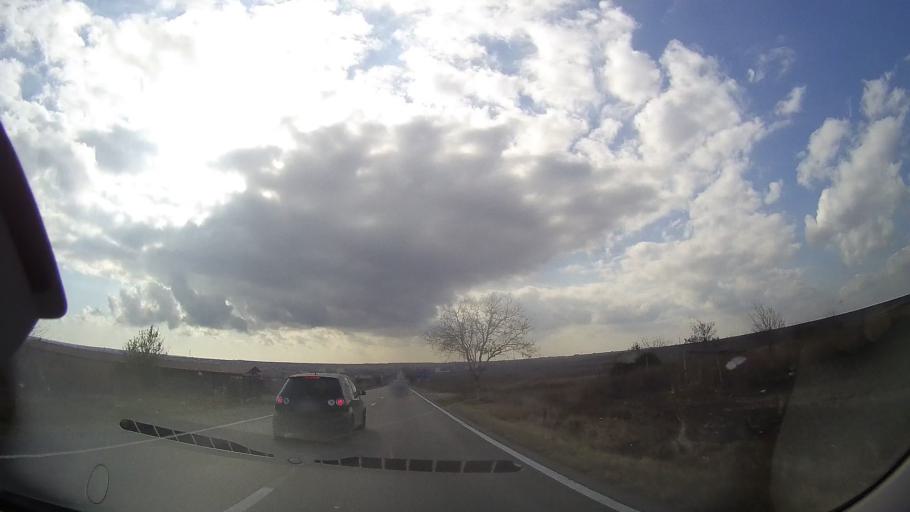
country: RO
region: Constanta
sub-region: Oras Techirghiol
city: Techirghiol
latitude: 44.0686
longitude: 28.5951
